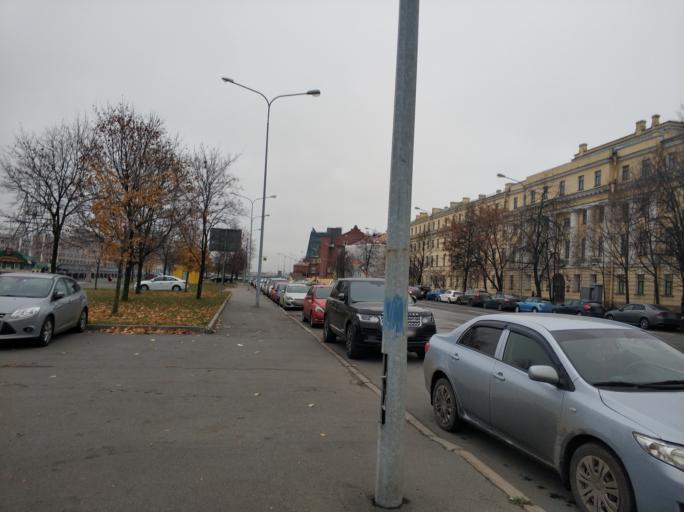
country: RU
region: Leningrad
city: Sampsonievskiy
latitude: 59.9666
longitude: 30.3334
